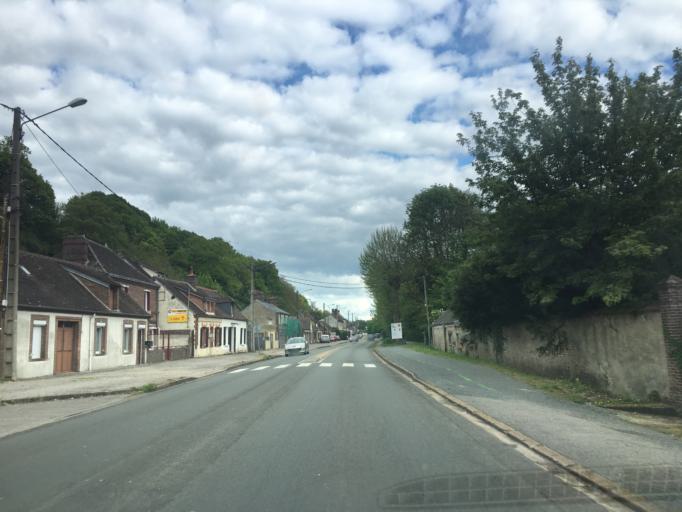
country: FR
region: Haute-Normandie
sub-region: Departement de l'Eure
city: La Madeleine-de-Nonancourt
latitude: 48.7673
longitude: 1.2070
